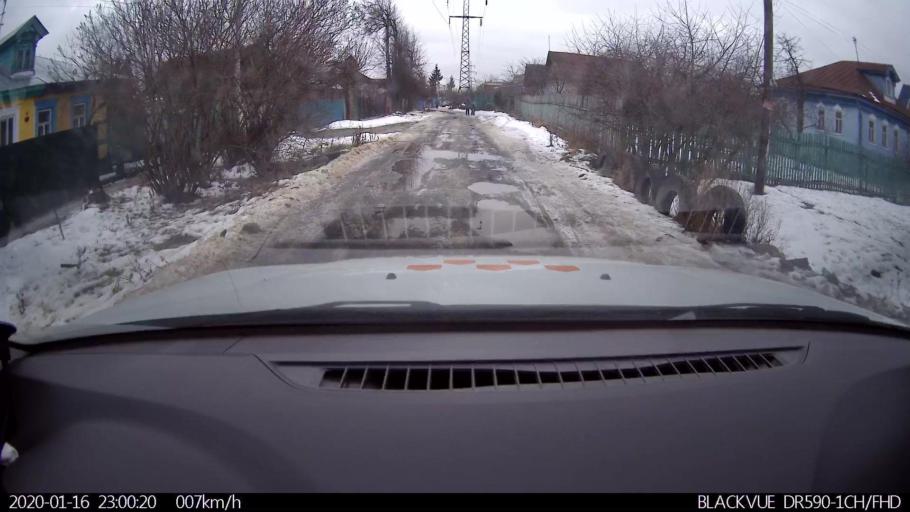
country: RU
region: Nizjnij Novgorod
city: Nizhniy Novgorod
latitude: 56.2860
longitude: 43.9059
